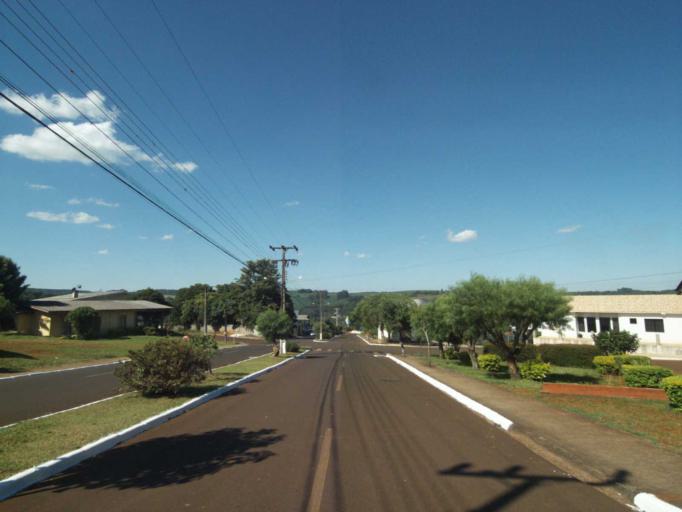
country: BR
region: Parana
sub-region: Laranjeiras Do Sul
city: Laranjeiras do Sul
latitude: -25.3833
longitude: -52.2060
